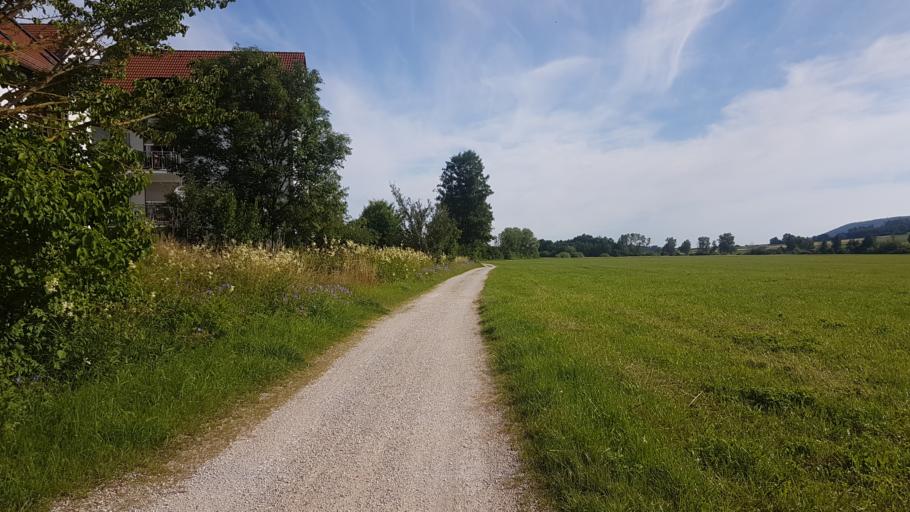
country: DE
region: Bavaria
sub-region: Regierungsbezirk Mittelfranken
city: Treuchtlingen
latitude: 48.9675
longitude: 10.9122
